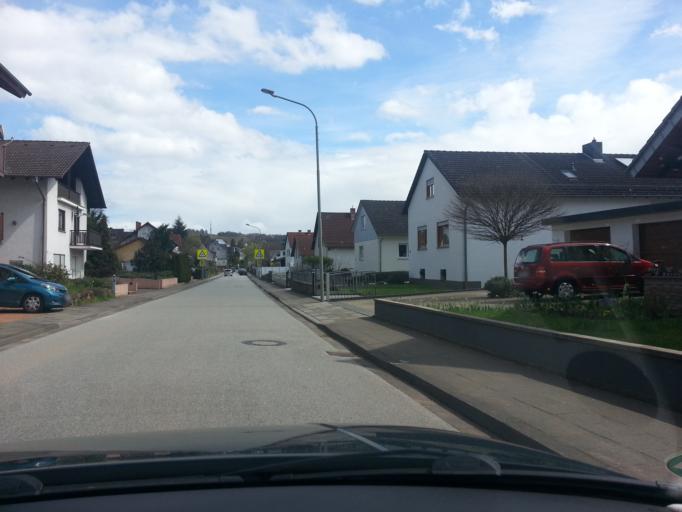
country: DE
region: Rheinland-Pfalz
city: Thaleischweiler-Froschen
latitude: 49.2643
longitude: 7.5703
